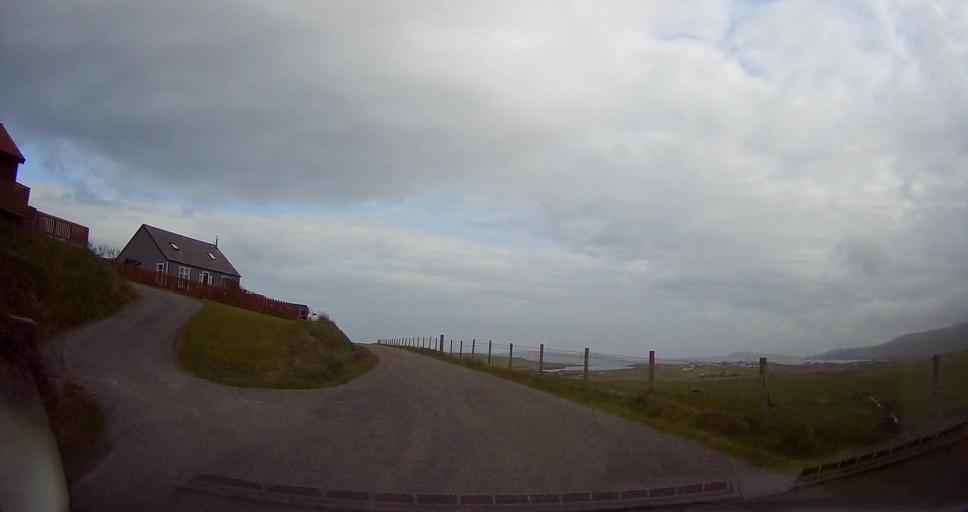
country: GB
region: Scotland
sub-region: Shetland Islands
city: Sandwick
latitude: 60.0509
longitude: -1.2221
